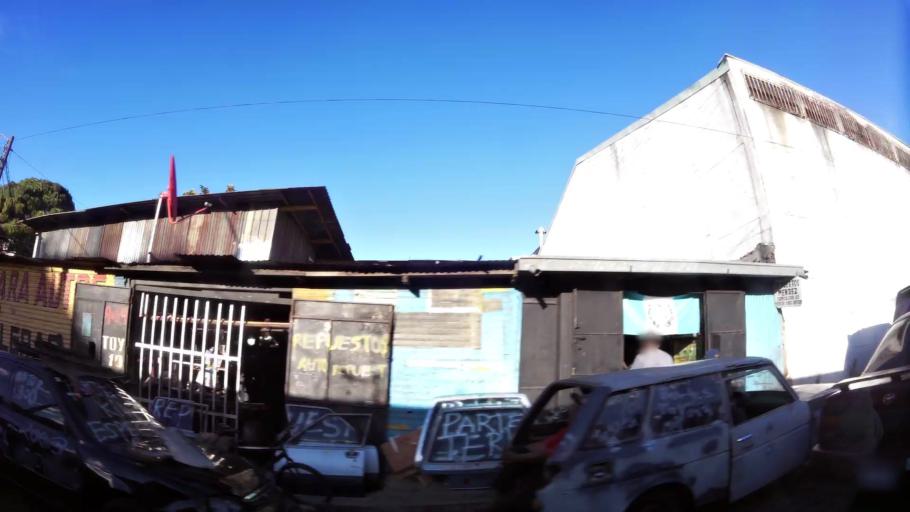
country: GT
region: Guatemala
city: Guatemala City
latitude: 14.6144
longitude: -90.5269
